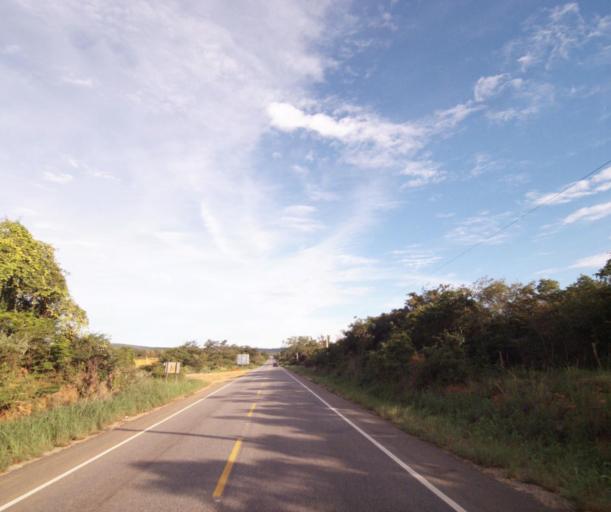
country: BR
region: Bahia
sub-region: Caetite
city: Caetite
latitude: -14.1217
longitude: -42.4243
